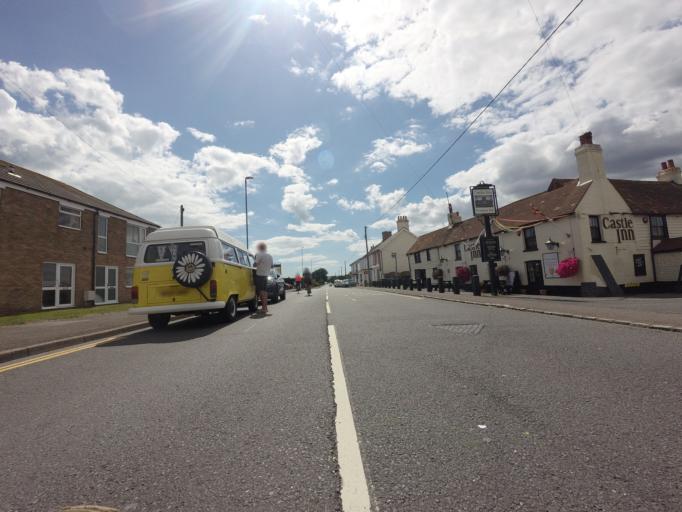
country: GB
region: England
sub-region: East Sussex
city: Pevensey
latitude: 50.8114
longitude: 0.3492
